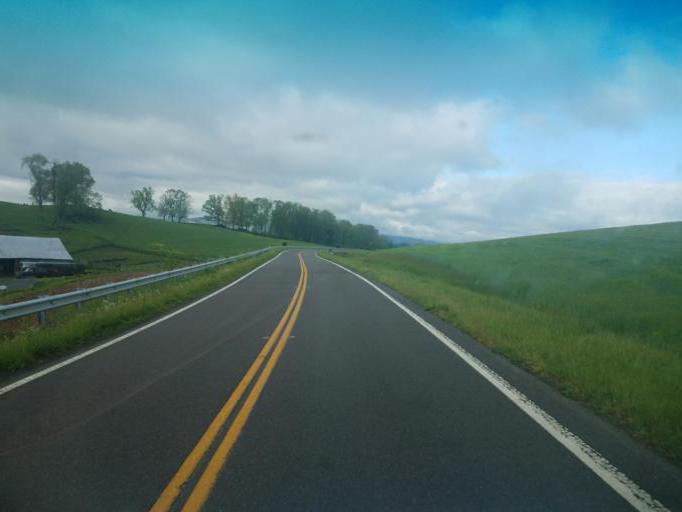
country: US
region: Virginia
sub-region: Washington County
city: Emory
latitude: 36.6989
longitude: -81.7957
